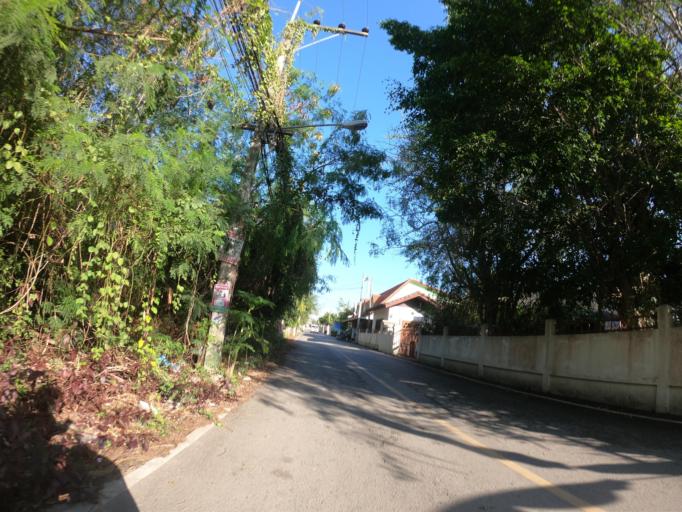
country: TH
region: Chiang Mai
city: San Sai
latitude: 18.8248
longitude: 99.0325
